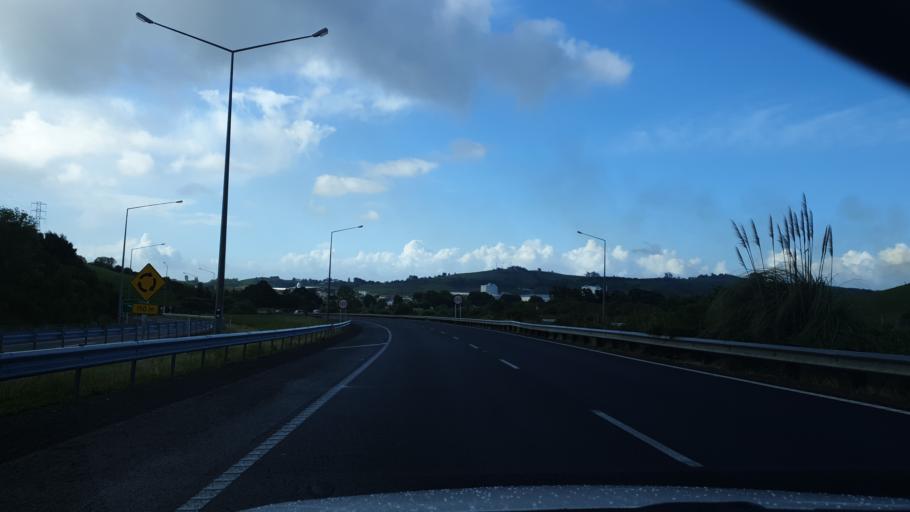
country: NZ
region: Auckland
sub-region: Auckland
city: Pukekohe East
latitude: -37.2373
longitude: 175.0205
